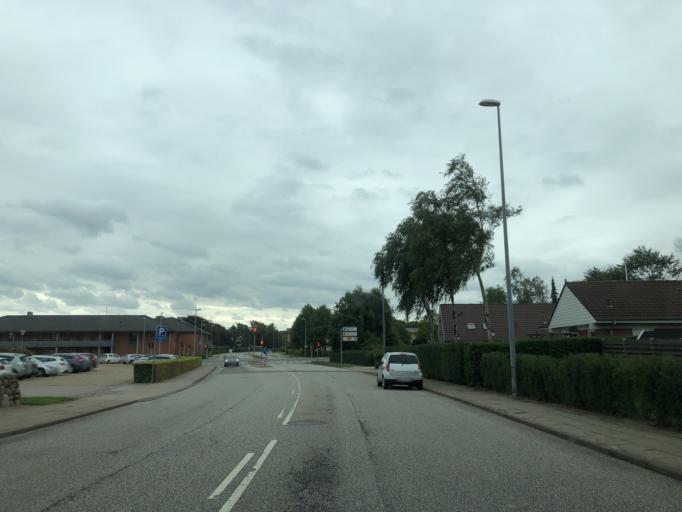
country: DK
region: Central Jutland
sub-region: Herning Kommune
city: Snejbjerg
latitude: 56.1343
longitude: 8.9047
